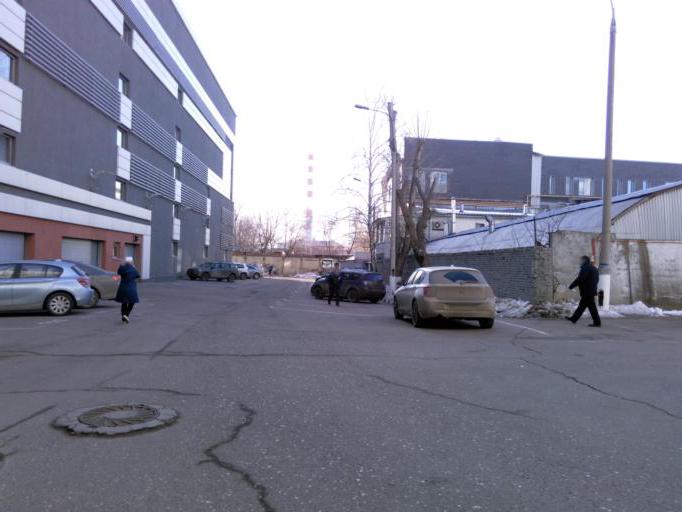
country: RU
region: Moscow
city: Zamoskvorech'ye
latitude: 55.7216
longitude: 37.6381
